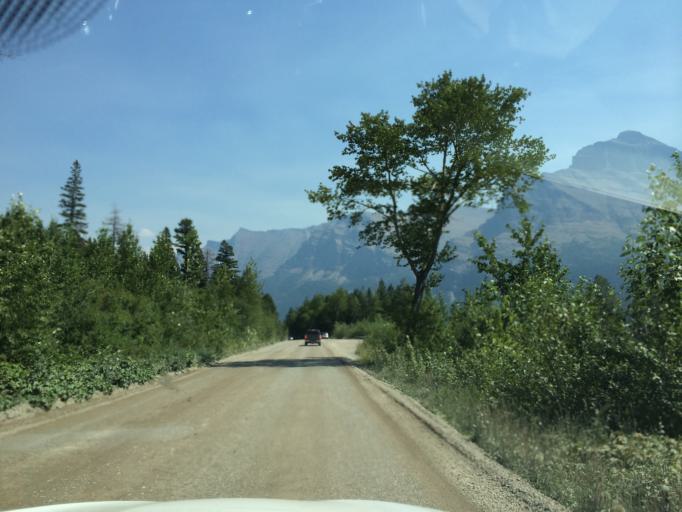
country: US
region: Montana
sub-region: Flathead County
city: Columbia Falls
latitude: 48.6765
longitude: -113.6424
